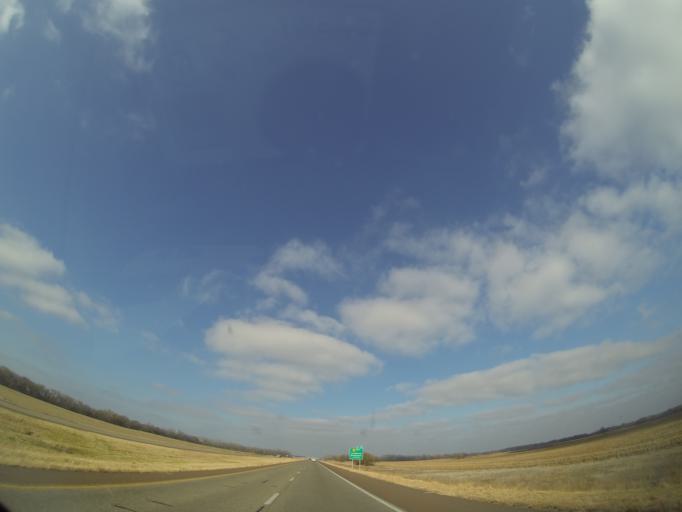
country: US
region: Kansas
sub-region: McPherson County
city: Lindsborg
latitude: 38.6047
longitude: -97.6212
